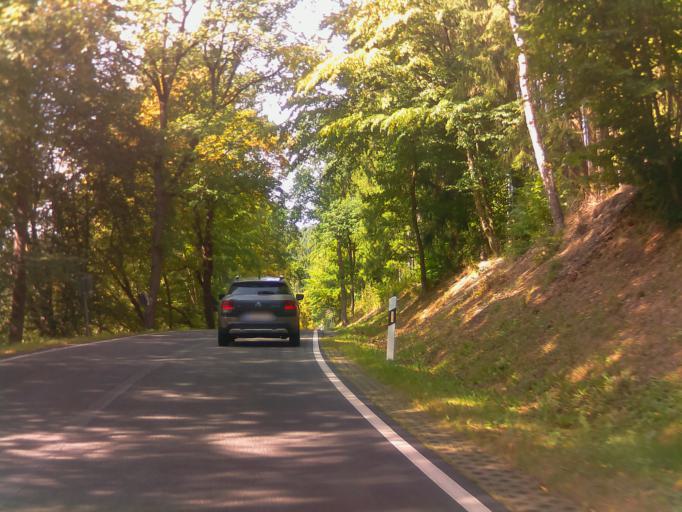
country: DE
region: Thuringia
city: Schwarza
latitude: 50.6506
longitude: 10.5156
